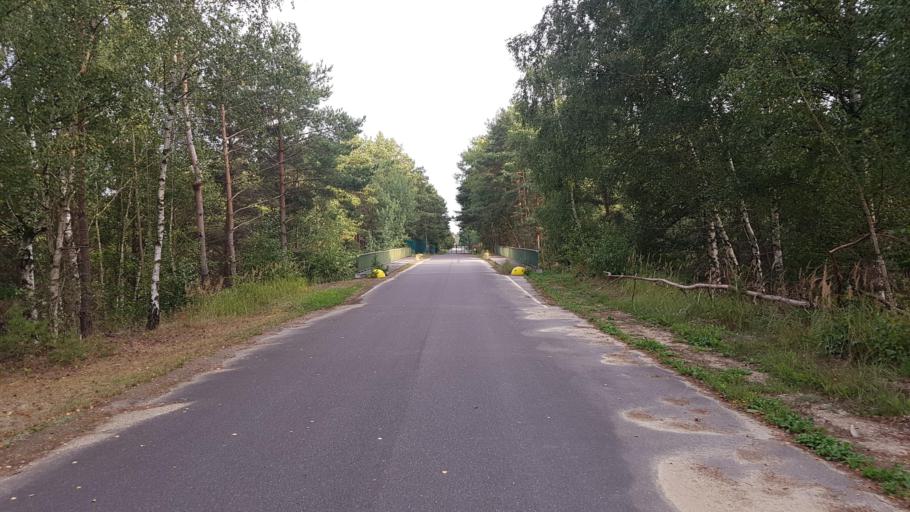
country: DE
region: Brandenburg
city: Schonborn
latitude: 51.6357
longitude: 13.5085
